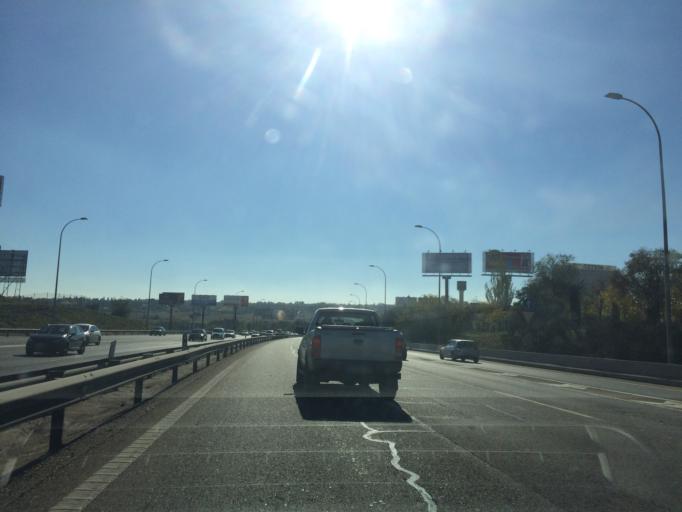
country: ES
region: Madrid
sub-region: Provincia de Madrid
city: San Sebastian de los Reyes
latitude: 40.5429
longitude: -3.6083
